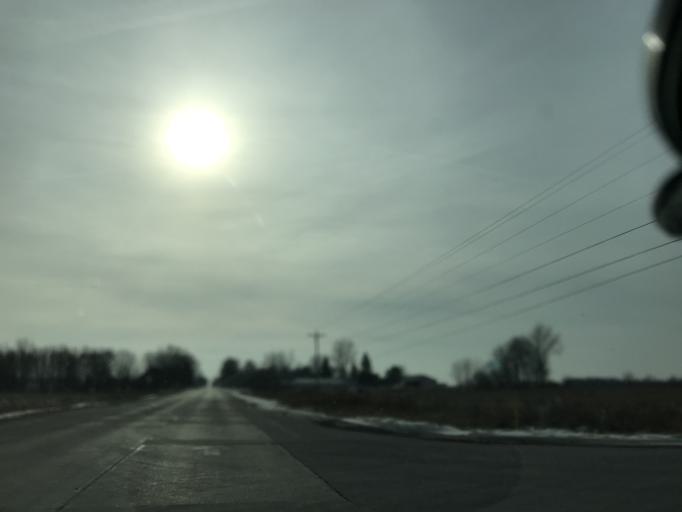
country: US
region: Michigan
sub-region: Ionia County
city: Lake Odessa
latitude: 42.8717
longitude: -85.0751
